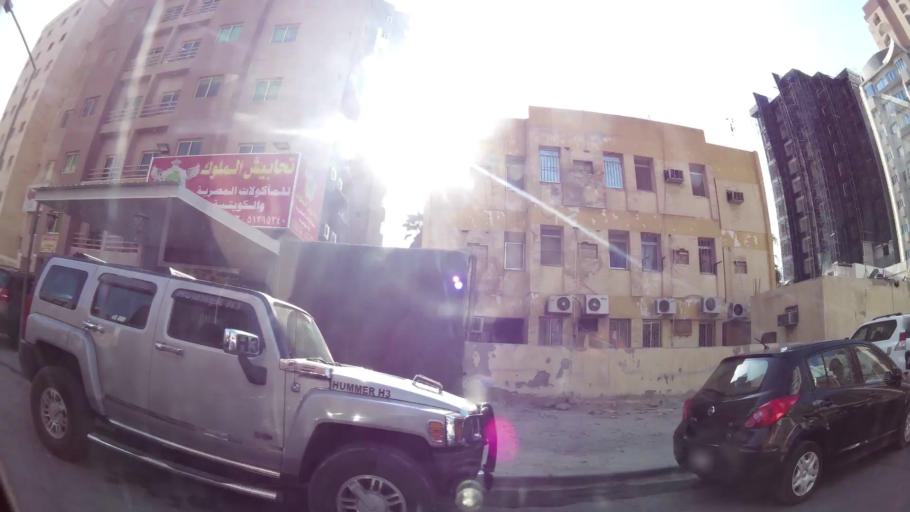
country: KW
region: Muhafazat Hawalli
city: As Salimiyah
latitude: 29.3444
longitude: 48.0930
